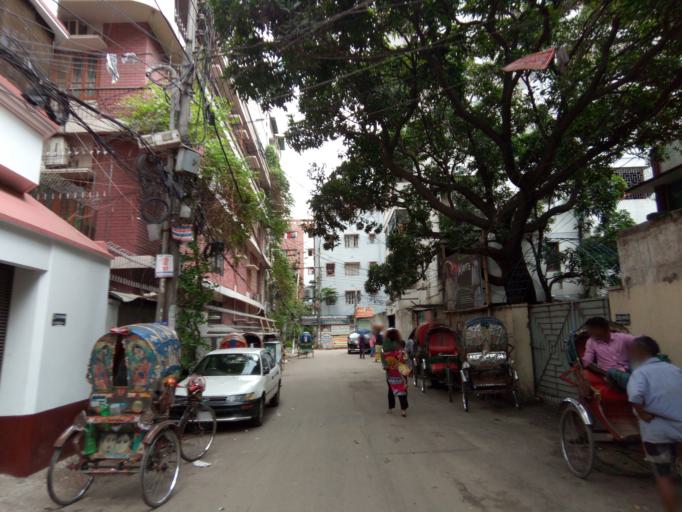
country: BD
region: Dhaka
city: Azimpur
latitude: 23.7496
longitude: 90.3831
